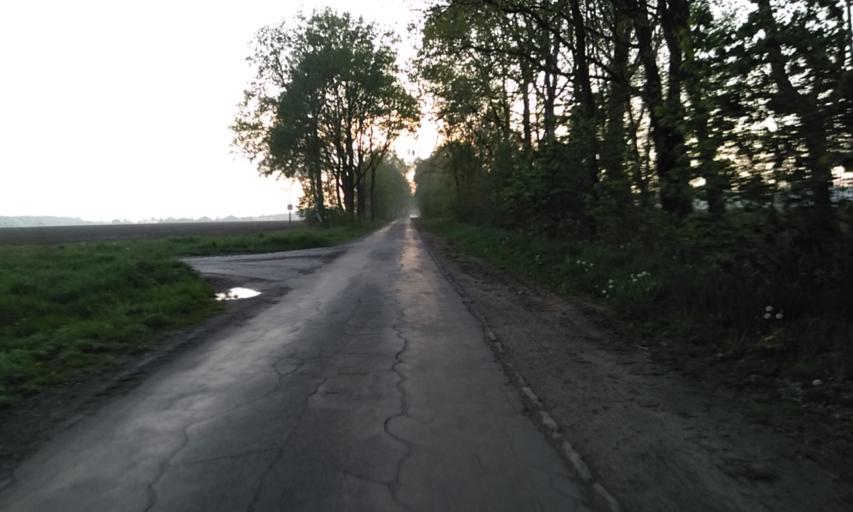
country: DE
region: Lower Saxony
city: Deinste
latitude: 53.4976
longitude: 9.4316
